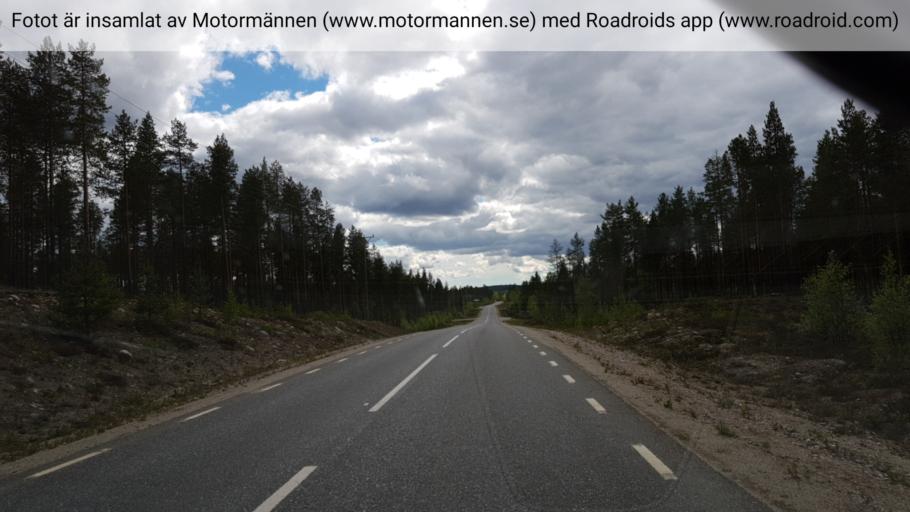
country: SE
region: Vaesterbotten
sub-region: Vindelns Kommun
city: Vindeln
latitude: 64.5109
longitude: 19.7937
